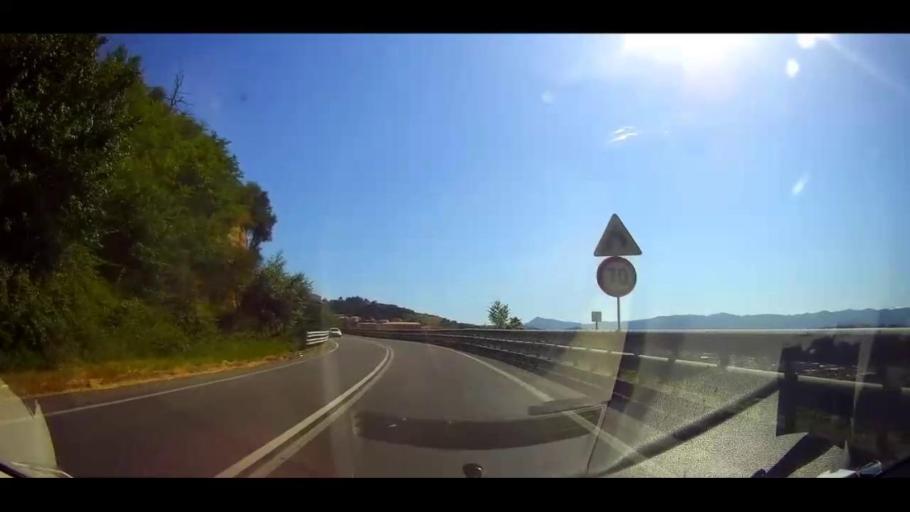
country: IT
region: Calabria
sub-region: Provincia di Cosenza
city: Cosenza
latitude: 39.2991
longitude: 16.2651
